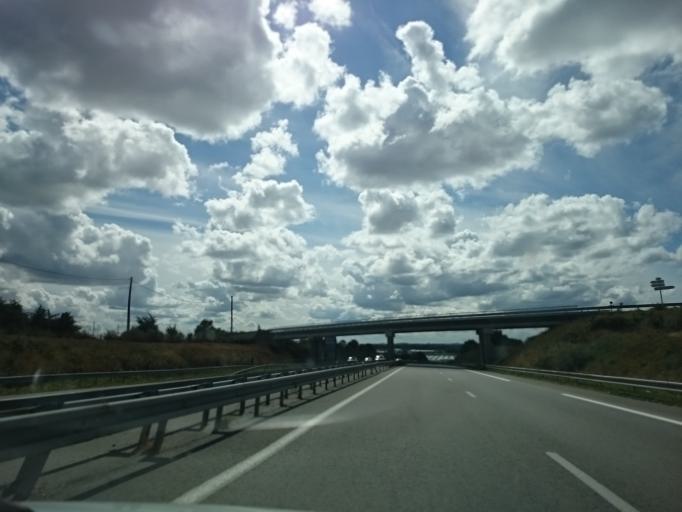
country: FR
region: Pays de la Loire
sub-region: Departement de la Loire-Atlantique
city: Thouare-sur-Loire
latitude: 47.3001
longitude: -1.4340
